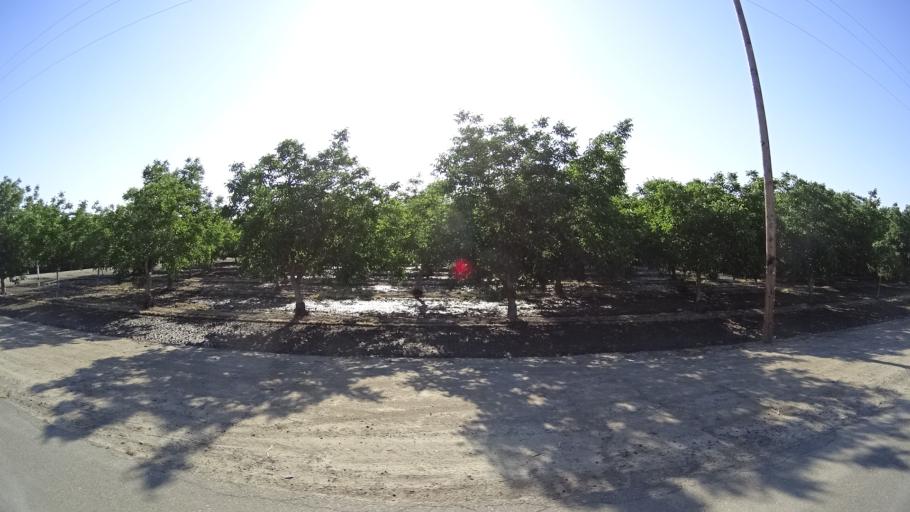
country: US
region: California
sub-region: Kings County
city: Armona
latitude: 36.3240
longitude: -119.7089
